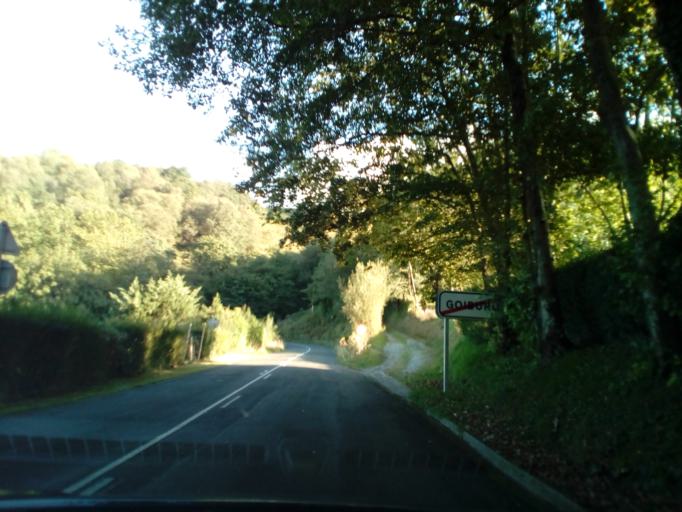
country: ES
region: Basque Country
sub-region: Provincia de Guipuzcoa
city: Urnieta
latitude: 43.2264
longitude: -1.9857
